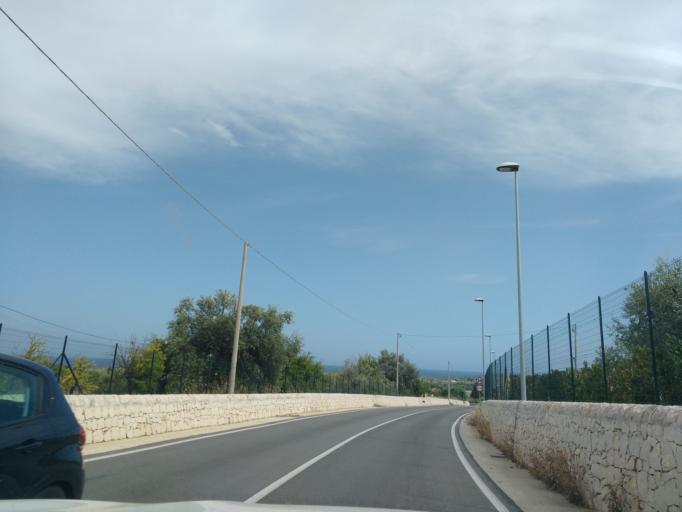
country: IT
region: Sicily
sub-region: Provincia di Siracusa
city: Noto
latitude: 36.8552
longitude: 15.0901
